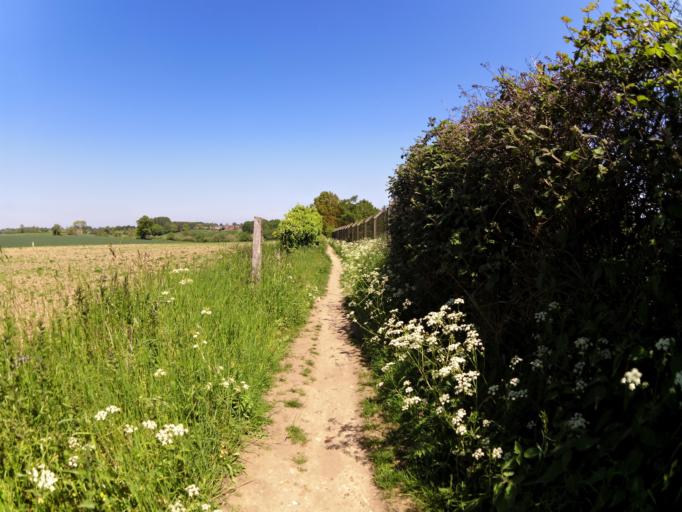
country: GB
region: England
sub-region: Essex
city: Mistley
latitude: 51.9802
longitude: 1.1465
